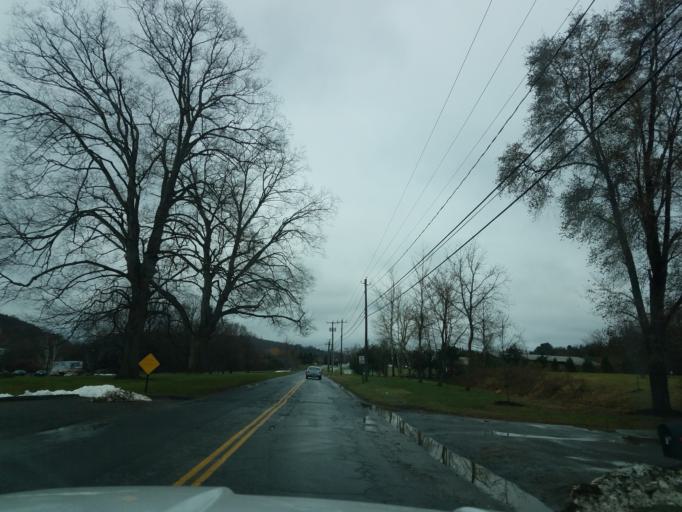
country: US
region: Connecticut
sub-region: Litchfield County
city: New Milford
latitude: 41.5515
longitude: -73.4105
